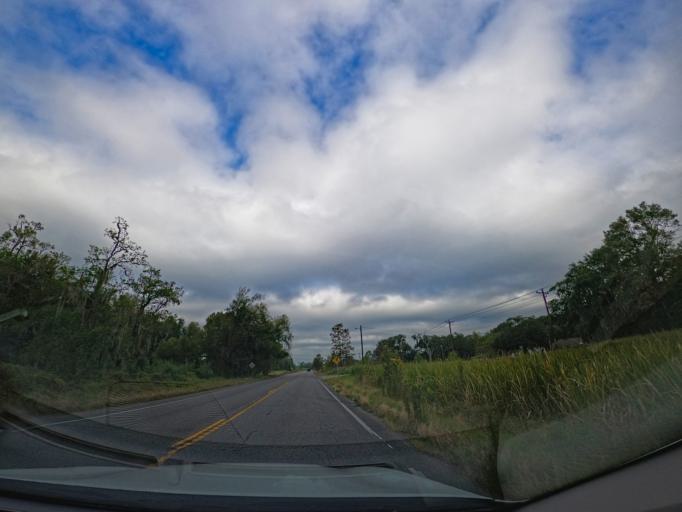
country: US
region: Louisiana
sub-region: Saint Mary Parish
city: Amelia
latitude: 29.6429
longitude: -90.9611
